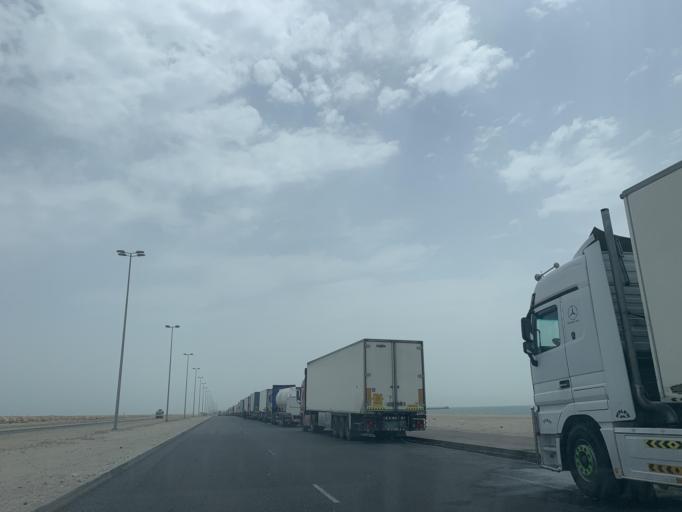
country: BH
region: Muharraq
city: Al Hadd
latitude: 26.2074
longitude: 50.7059
